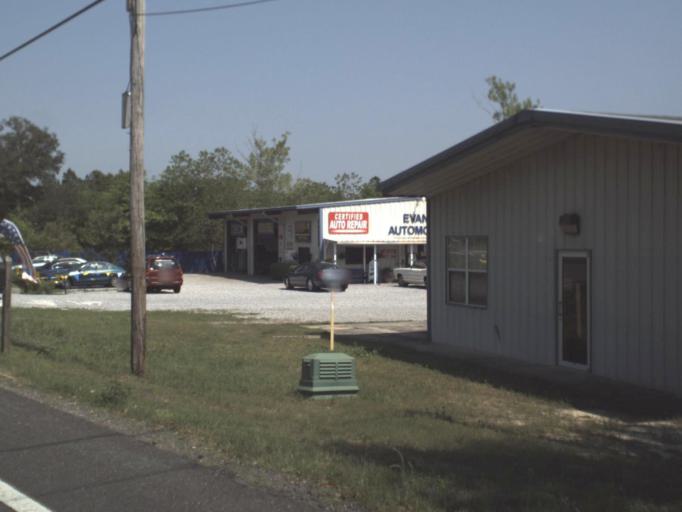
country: US
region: Florida
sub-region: Escambia County
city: Myrtle Grove
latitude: 30.4011
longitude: -87.3816
